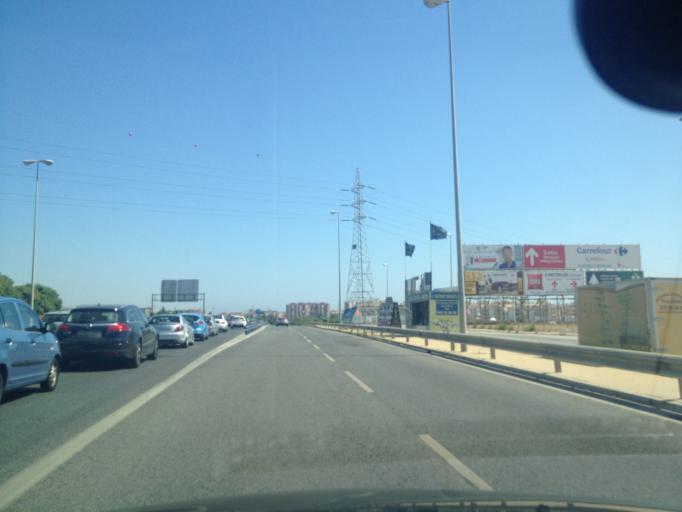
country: ES
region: Andalusia
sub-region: Provincia de Malaga
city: Malaga
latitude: 36.7131
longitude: -4.4704
